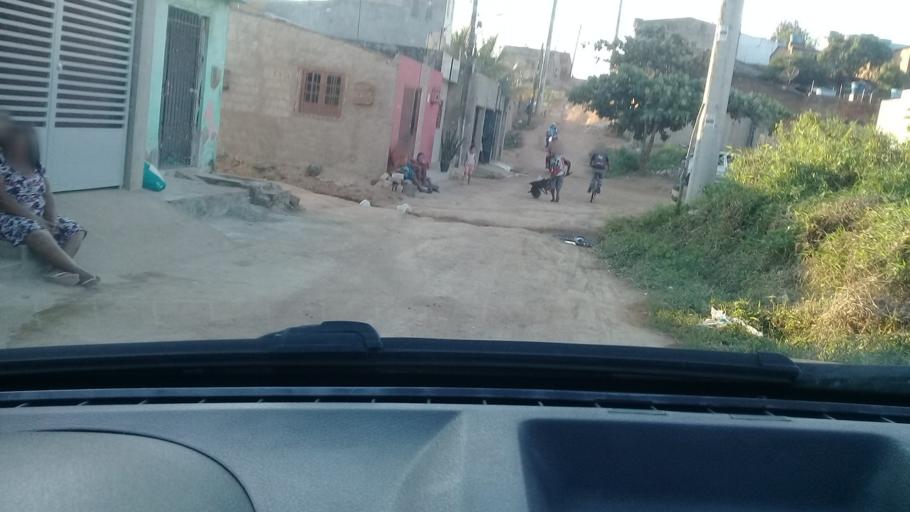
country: BR
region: Pernambuco
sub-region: Vitoria De Santo Antao
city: Vitoria de Santo Antao
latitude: -8.1327
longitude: -35.2923
